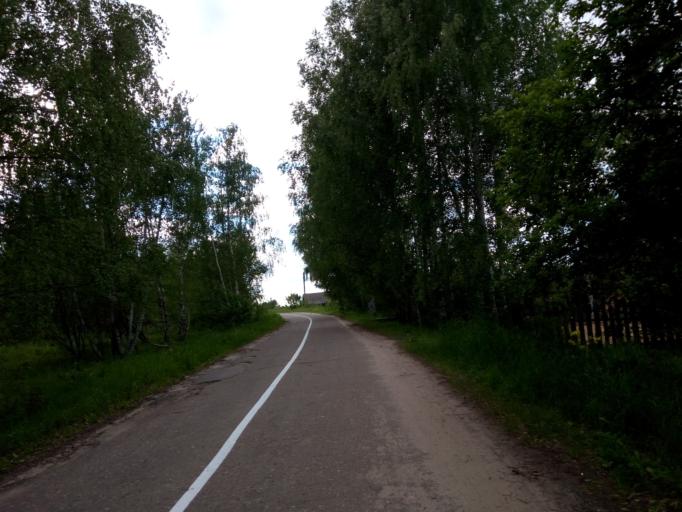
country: RU
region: Nizjnij Novgorod
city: Voskresenskoye
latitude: 56.7796
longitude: 45.5247
